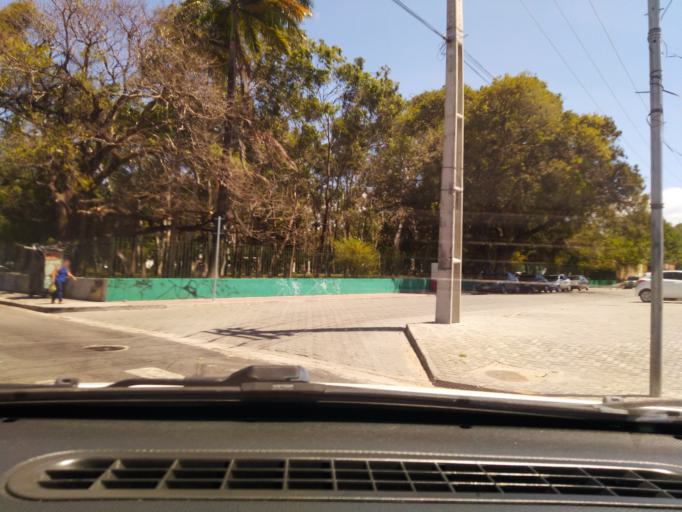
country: BR
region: Ceara
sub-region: Eusebio
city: Eusebio
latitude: -3.8140
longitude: -38.4989
